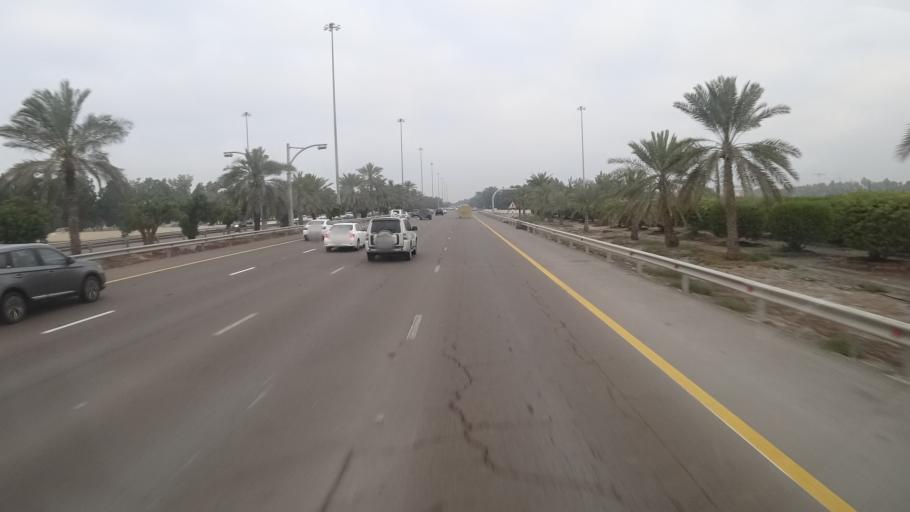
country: AE
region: Abu Dhabi
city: Abu Dhabi
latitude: 24.3541
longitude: 54.5685
